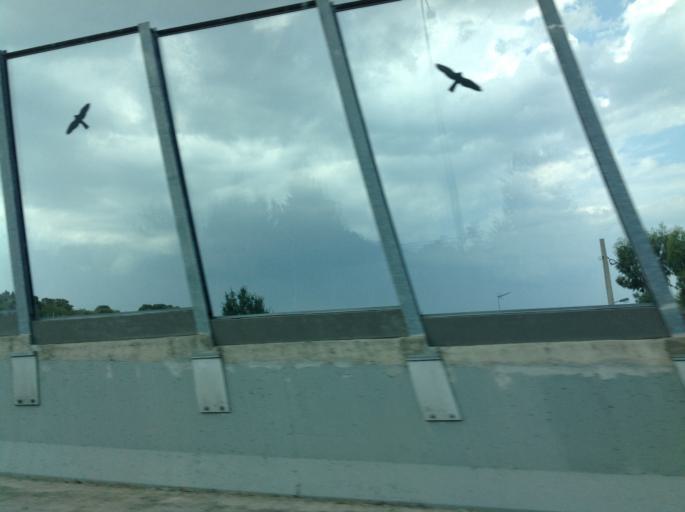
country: GR
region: Attica
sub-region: Nomarchia Anatolikis Attikis
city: Leondarion
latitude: 37.9977
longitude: 23.8441
